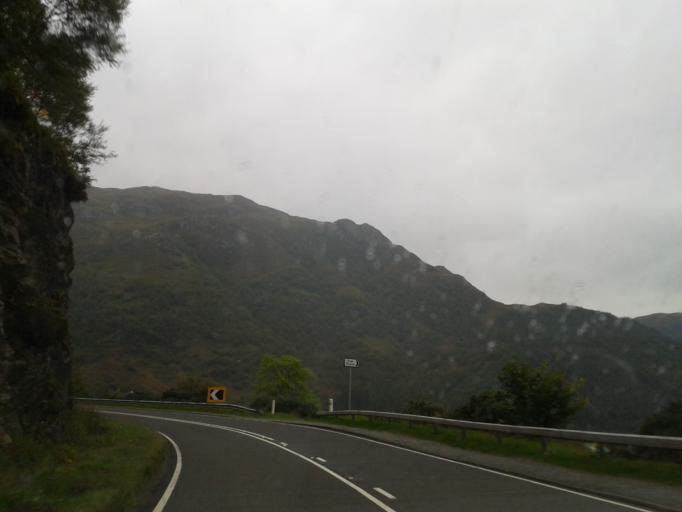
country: GB
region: Scotland
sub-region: Highland
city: Fort William
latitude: 57.2164
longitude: -5.4225
